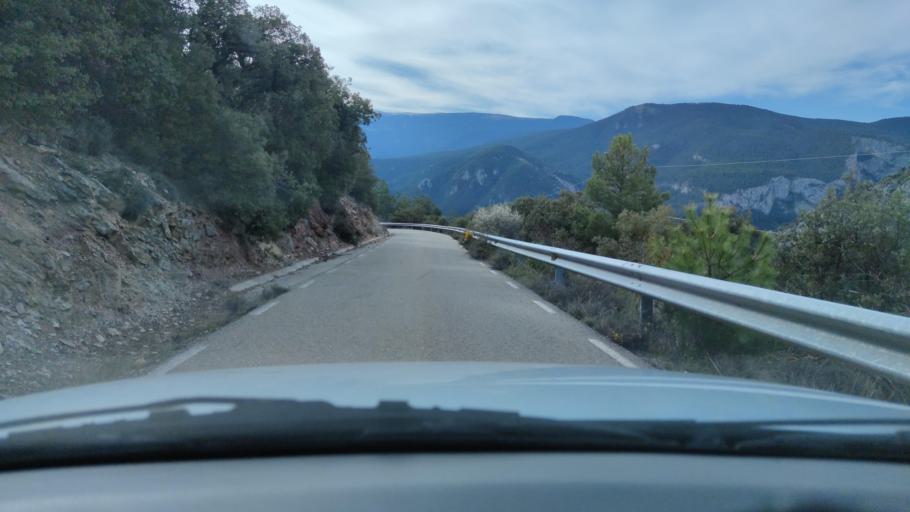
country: ES
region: Catalonia
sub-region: Provincia de Lleida
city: la Seu d'Urgell
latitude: 42.2510
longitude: 1.4121
